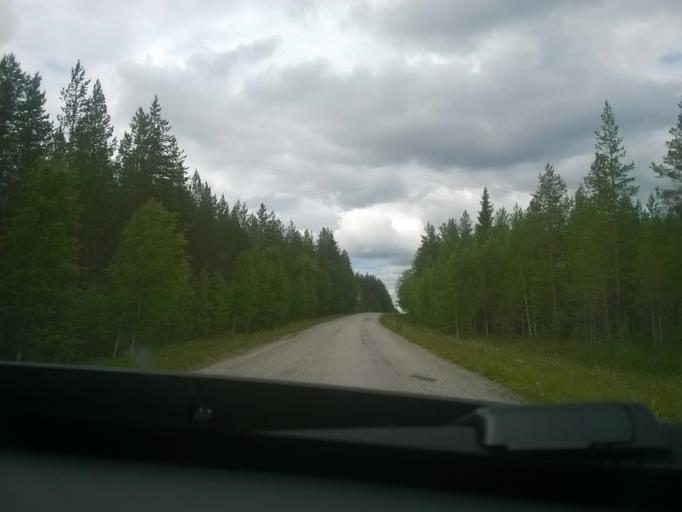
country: FI
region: Kainuu
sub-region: Kehys-Kainuu
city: Kuhmo
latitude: 64.3885
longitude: 29.7891
